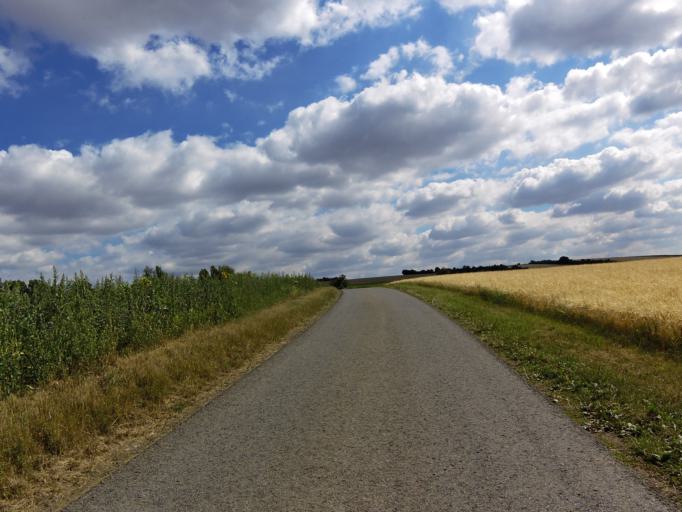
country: DE
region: Bavaria
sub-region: Regierungsbezirk Unterfranken
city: Gerbrunn
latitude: 49.7785
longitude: 10.0158
